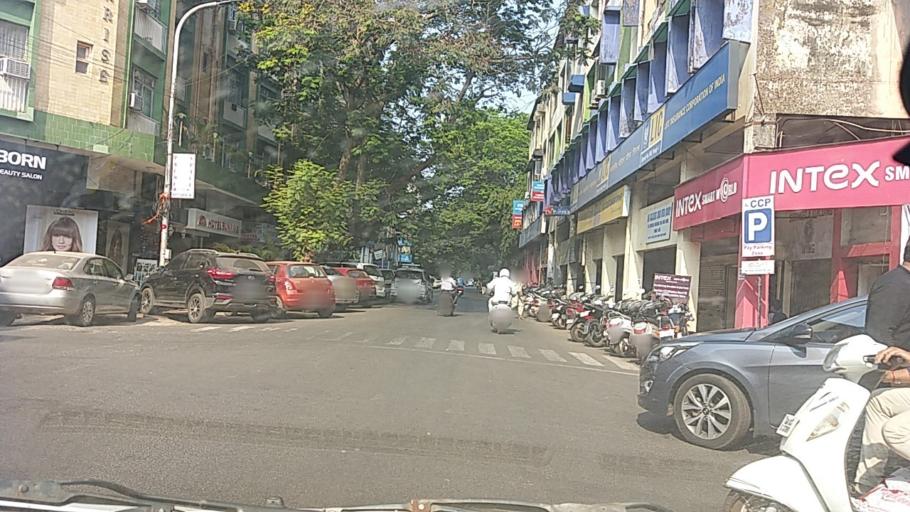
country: IN
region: Goa
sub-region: North Goa
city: Panaji
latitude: 15.4959
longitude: 73.8226
